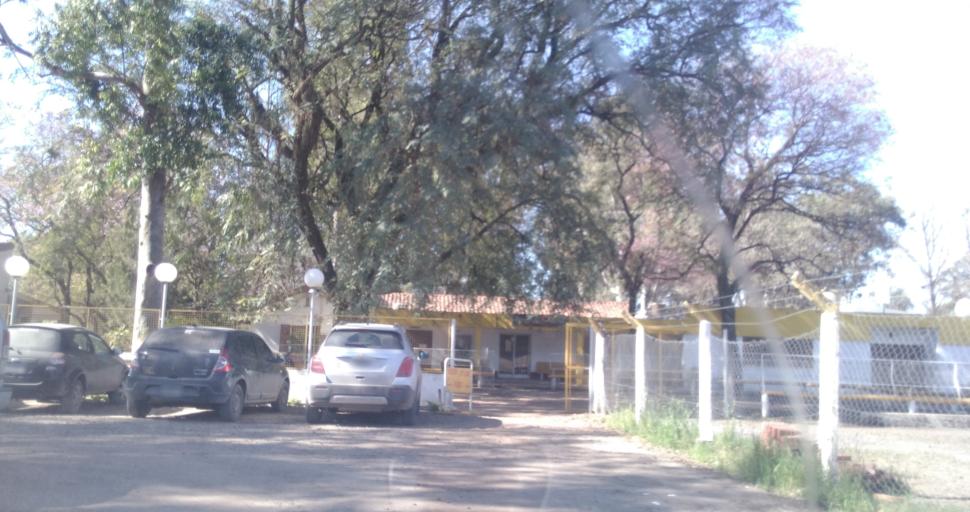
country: AR
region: Chaco
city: Resistencia
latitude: -27.4661
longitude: -58.9828
